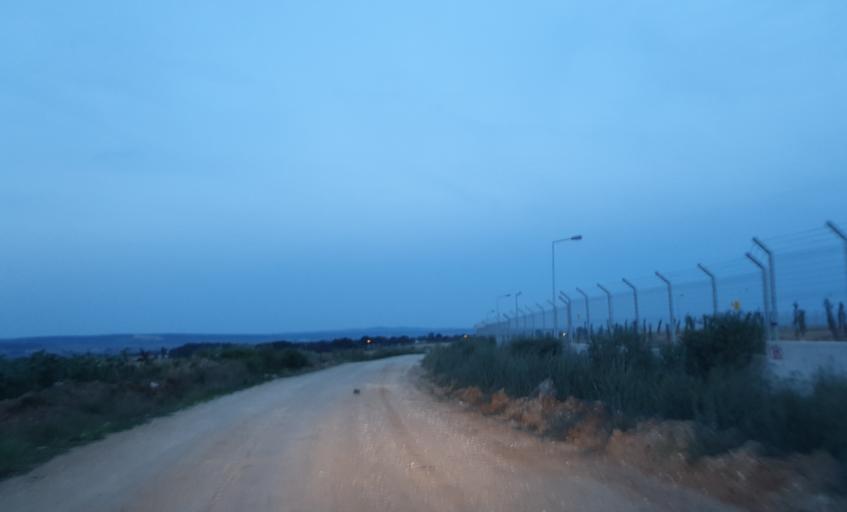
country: TR
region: Kirklareli
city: Vize
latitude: 41.5179
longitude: 27.7612
